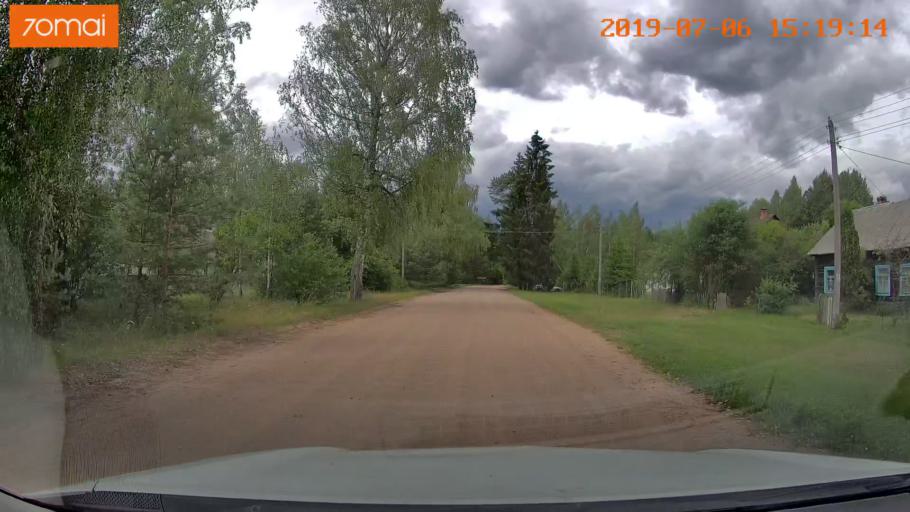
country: BY
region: Minsk
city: Ivyanyets
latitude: 53.9960
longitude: 26.6472
